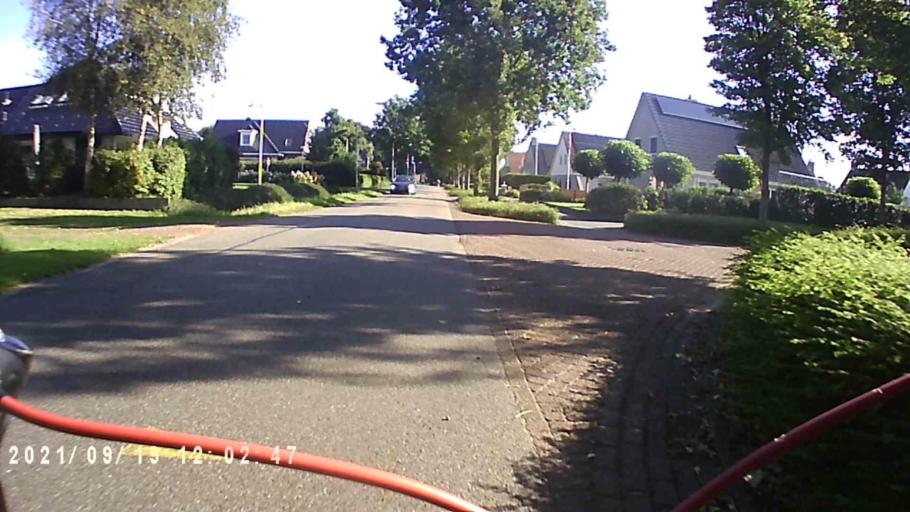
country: NL
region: Groningen
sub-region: Gemeente Slochteren
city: Slochteren
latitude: 53.2306
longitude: 6.8091
